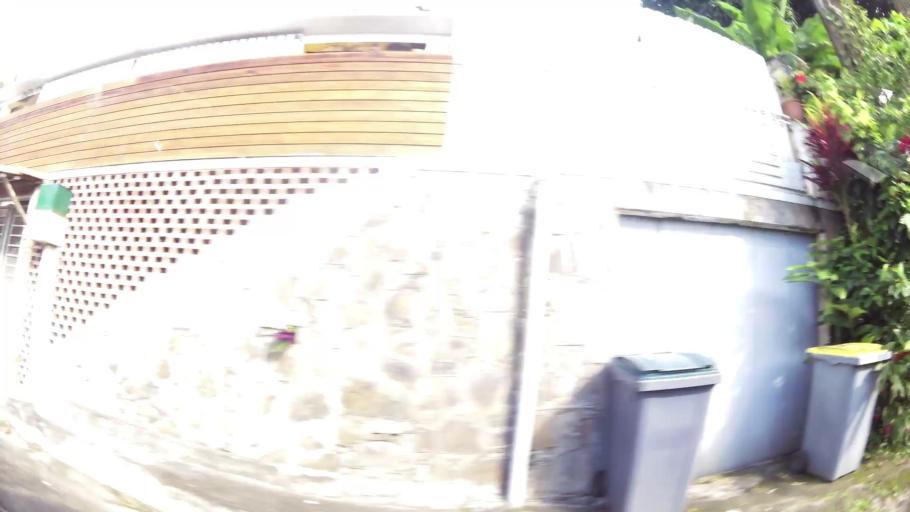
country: MQ
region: Martinique
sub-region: Martinique
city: Saint-Joseph
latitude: 14.6580
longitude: -61.0845
